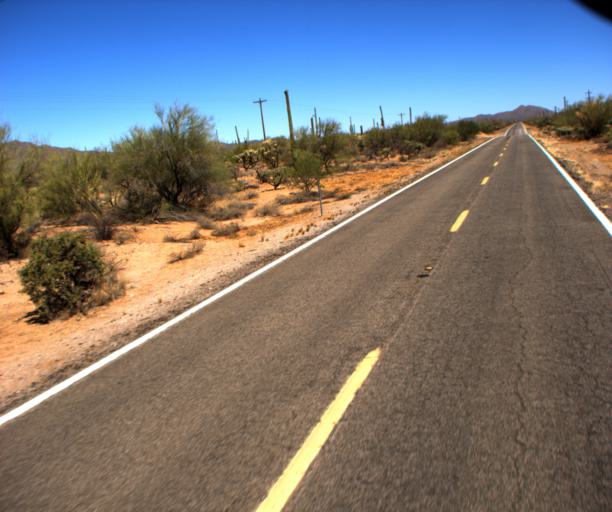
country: US
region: Arizona
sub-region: Pima County
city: Sells
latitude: 32.1258
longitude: -112.0862
